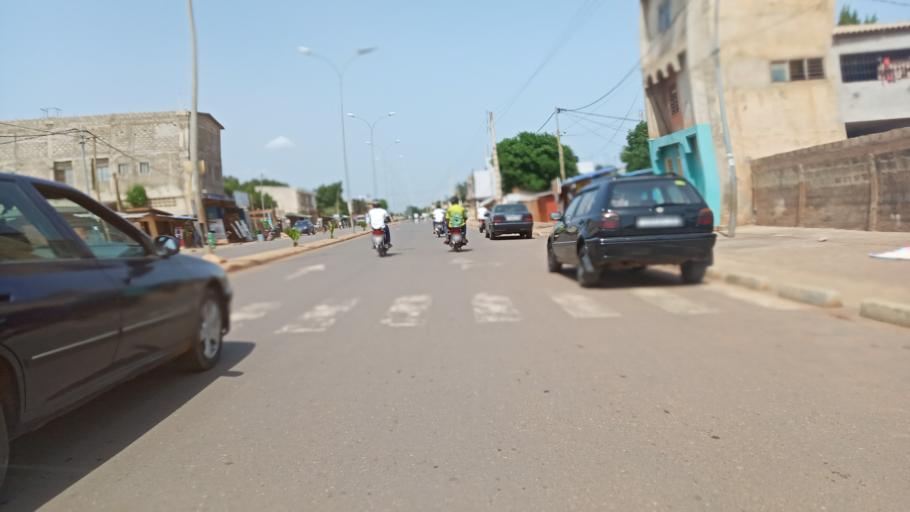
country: TG
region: Maritime
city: Lome
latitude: 6.2257
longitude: 1.1979
